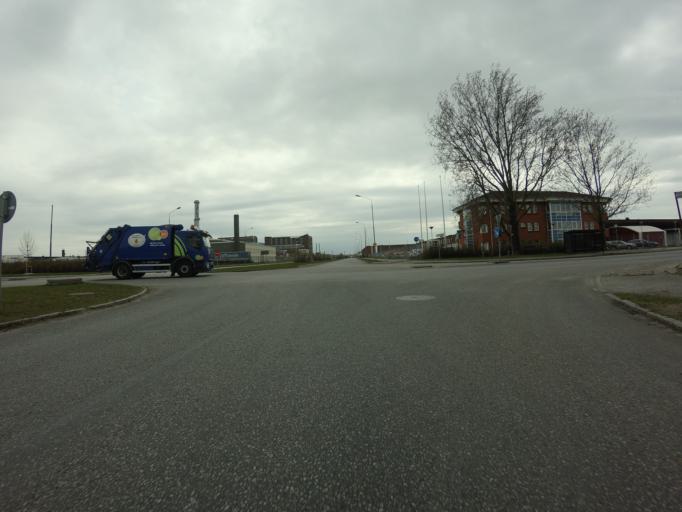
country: SE
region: Skane
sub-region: Burlovs Kommun
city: Arloev
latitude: 55.6297
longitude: 13.0361
